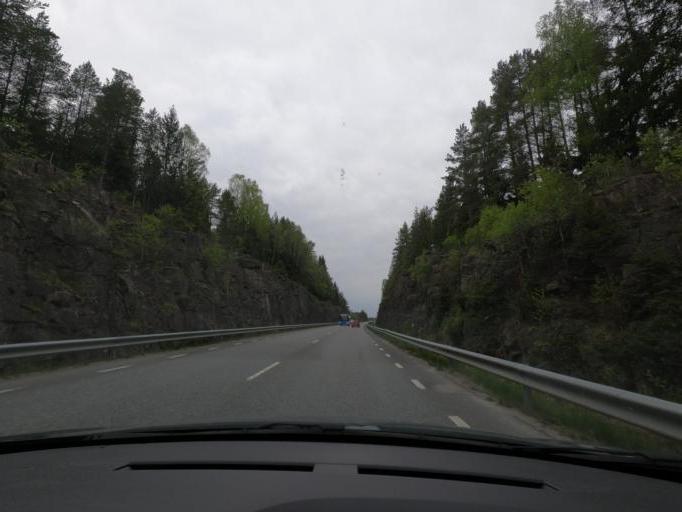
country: SE
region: Vaestra Goetaland
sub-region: Tranemo Kommun
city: Langhem
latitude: 57.5737
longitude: 13.2297
